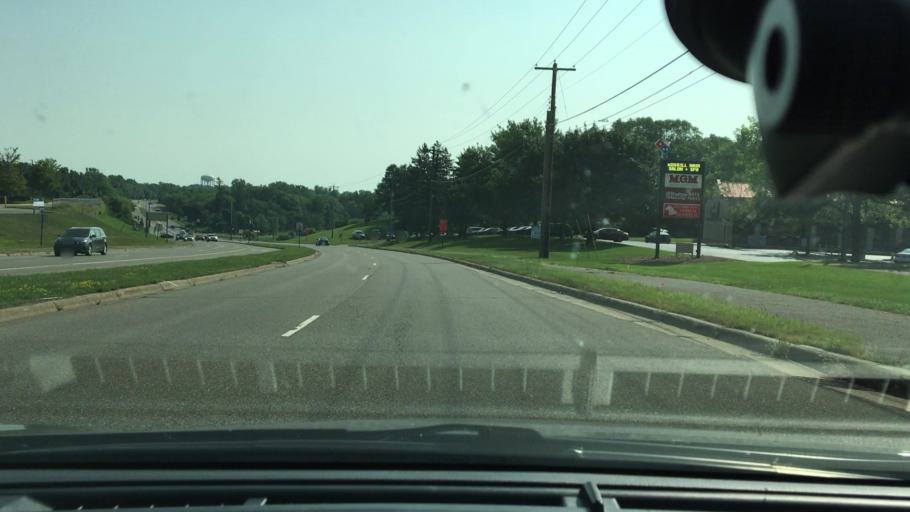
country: US
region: Minnesota
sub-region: Hennepin County
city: Plymouth
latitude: 45.0279
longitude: -93.4483
